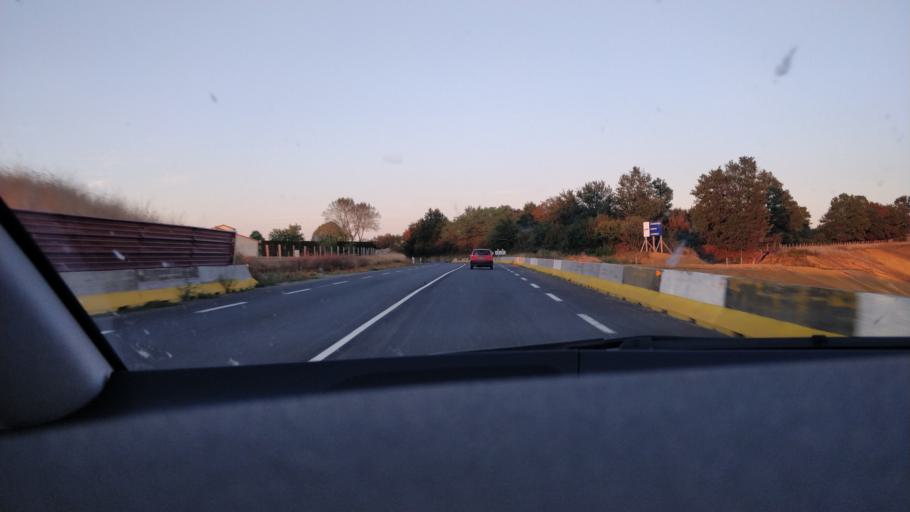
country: FR
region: Poitou-Charentes
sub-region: Departement de la Charente
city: Loubert
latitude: 45.8778
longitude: 0.5624
